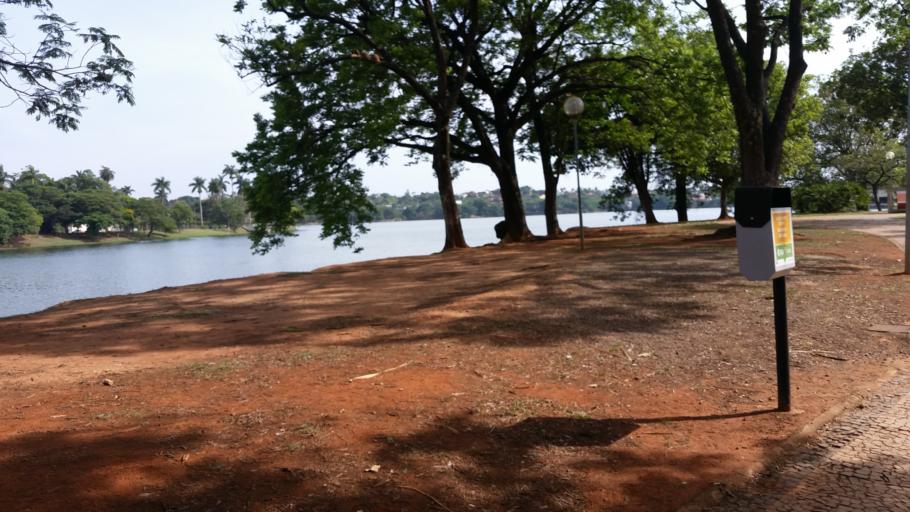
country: BR
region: Minas Gerais
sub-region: Belo Horizonte
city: Belo Horizonte
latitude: -19.8587
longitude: -43.9798
